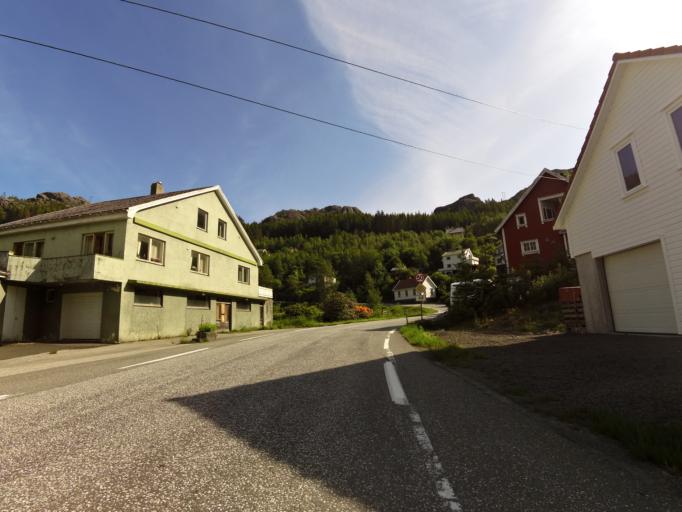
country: NO
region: Rogaland
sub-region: Sokndal
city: Hauge i Dalane
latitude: 58.3165
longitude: 6.3451
